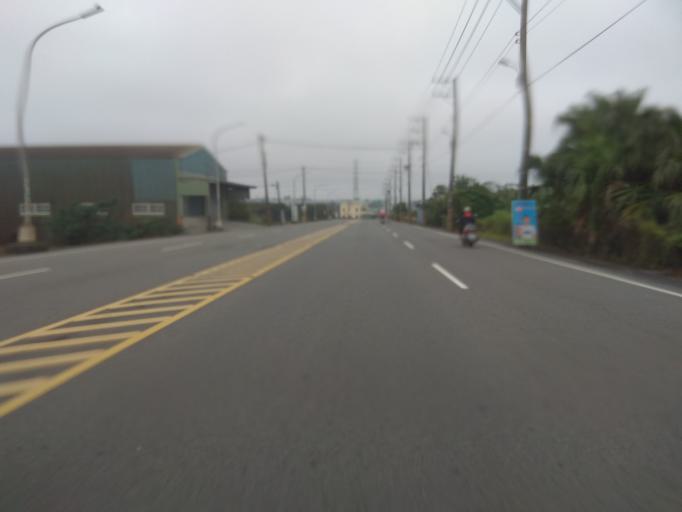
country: TW
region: Taiwan
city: Taoyuan City
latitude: 25.0173
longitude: 121.1266
